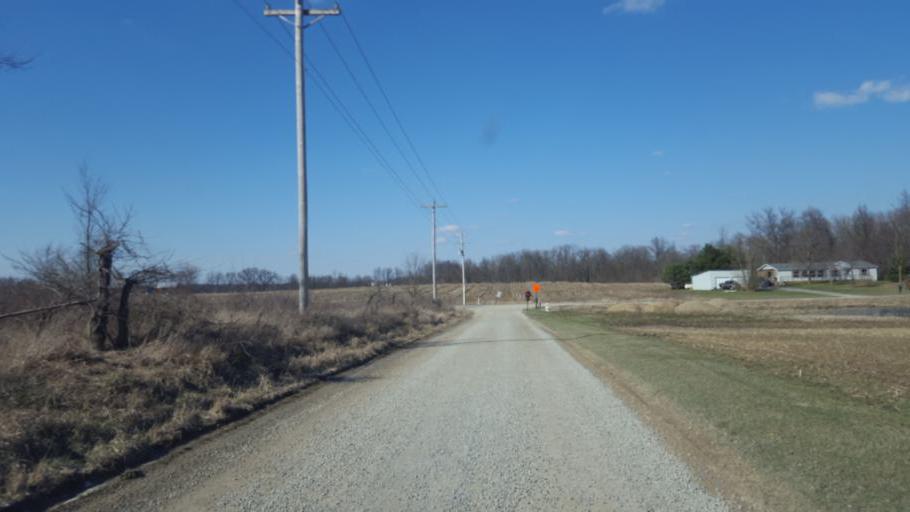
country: US
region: Ohio
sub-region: Morrow County
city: Mount Gilead
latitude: 40.5062
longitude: -82.7715
